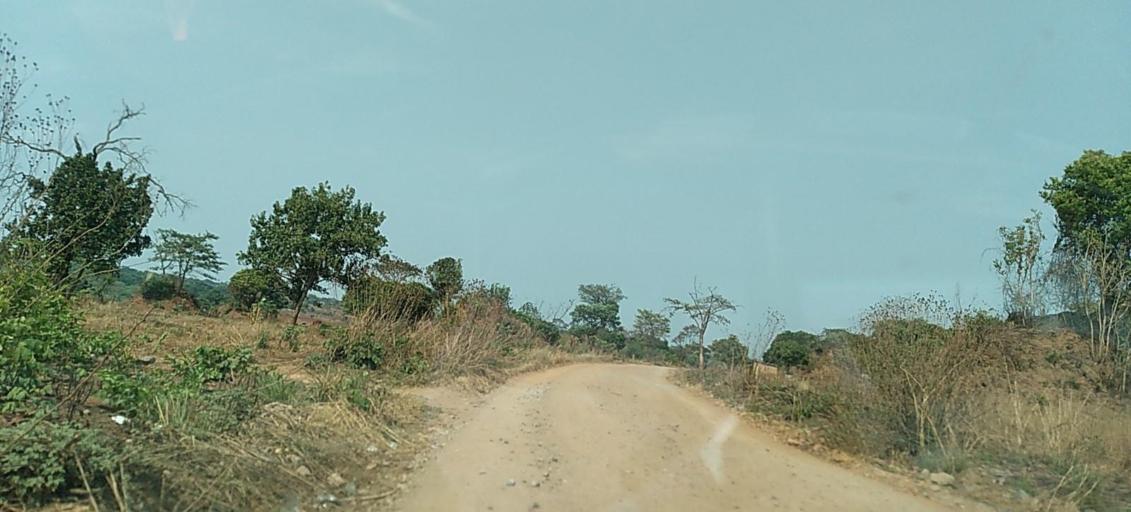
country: ZM
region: Copperbelt
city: Chililabombwe
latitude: -12.3387
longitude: 27.7203
